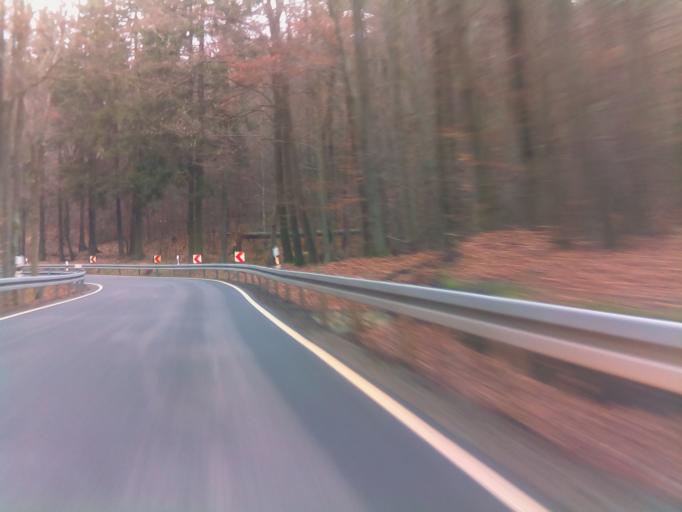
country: DE
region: Bavaria
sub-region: Regierungsbezirk Unterfranken
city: Miltenberg
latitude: 49.6888
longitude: 9.2933
